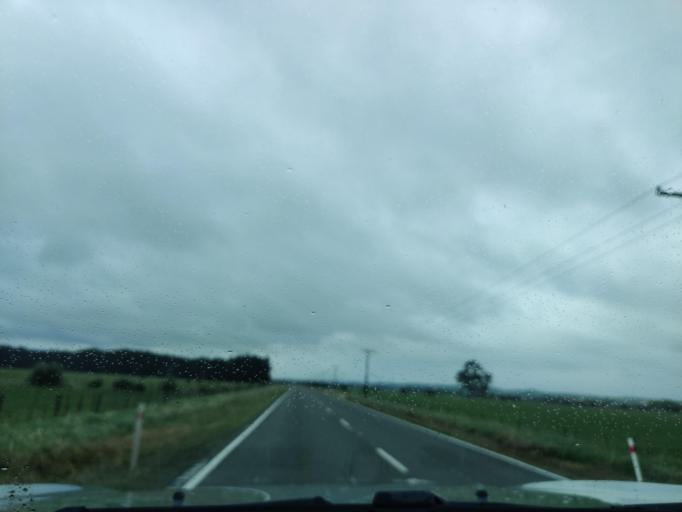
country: NZ
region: Hawke's Bay
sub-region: Hastings District
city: Hastings
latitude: -40.0097
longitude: 176.3783
